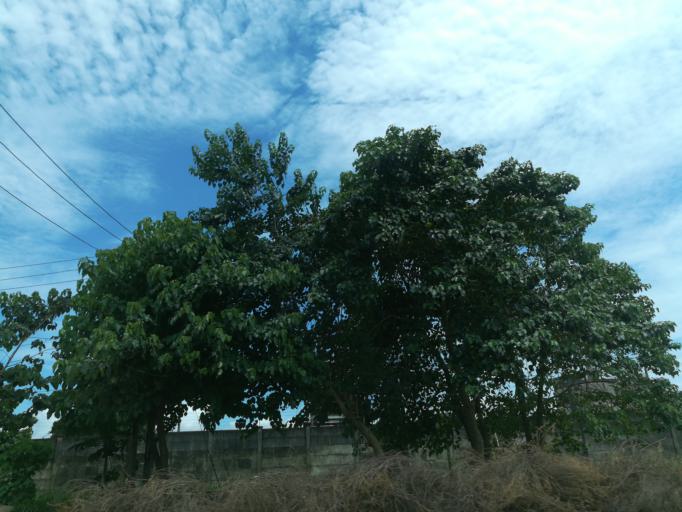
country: NG
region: Lagos
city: Ebute Ikorodu
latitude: 6.5722
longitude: 3.4844
